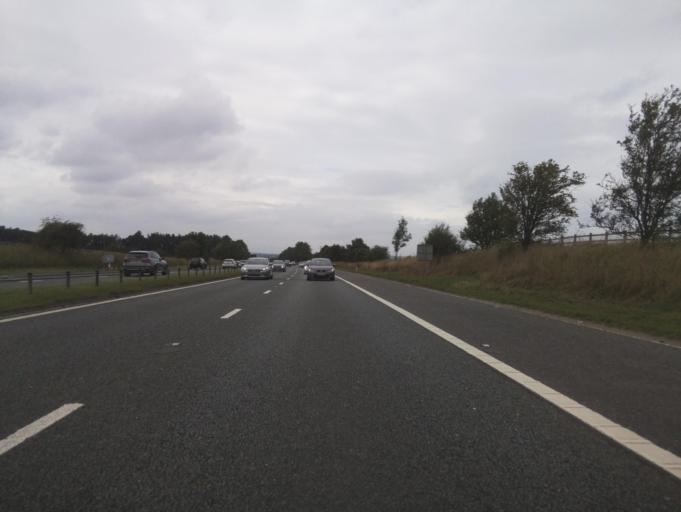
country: GB
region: England
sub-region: County Durham
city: Chester-le-Street
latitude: 54.8539
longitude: -1.5401
